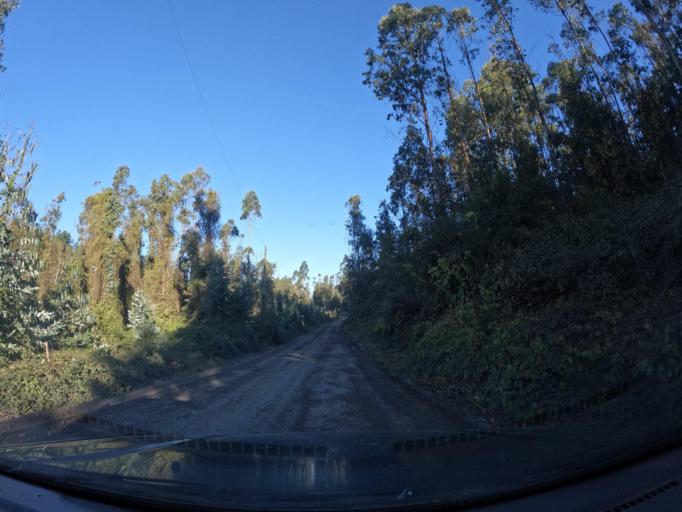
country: CL
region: Biobio
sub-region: Provincia de Concepcion
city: Chiguayante
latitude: -37.0230
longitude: -72.8874
